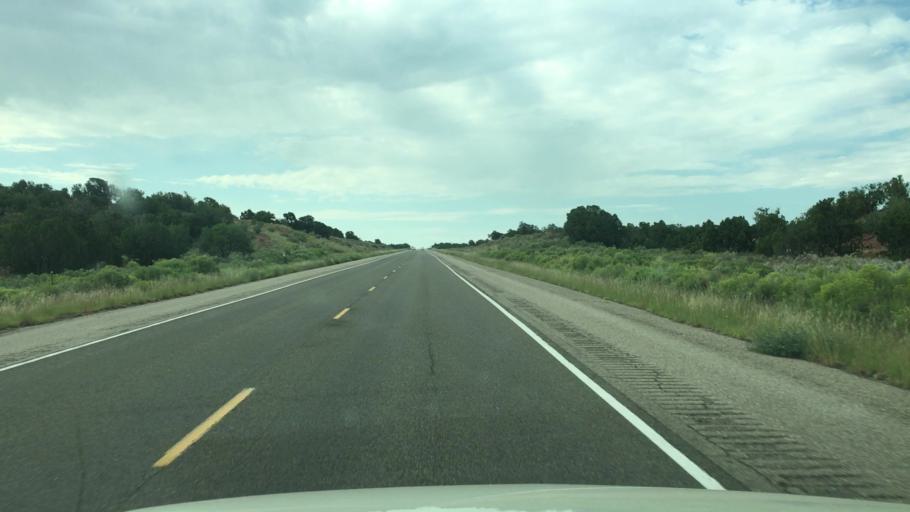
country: US
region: New Mexico
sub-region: Santa Fe County
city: Eldorado at Santa Fe
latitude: 35.2351
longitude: -105.8041
